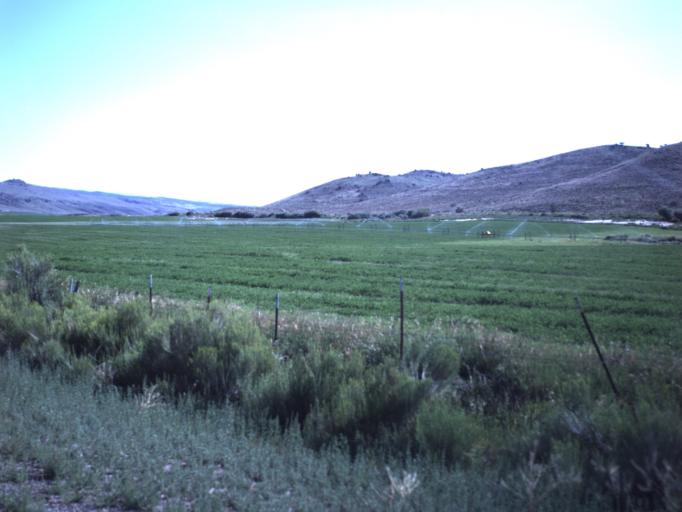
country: US
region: Utah
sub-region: Wayne County
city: Loa
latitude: 38.4411
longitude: -111.6158
